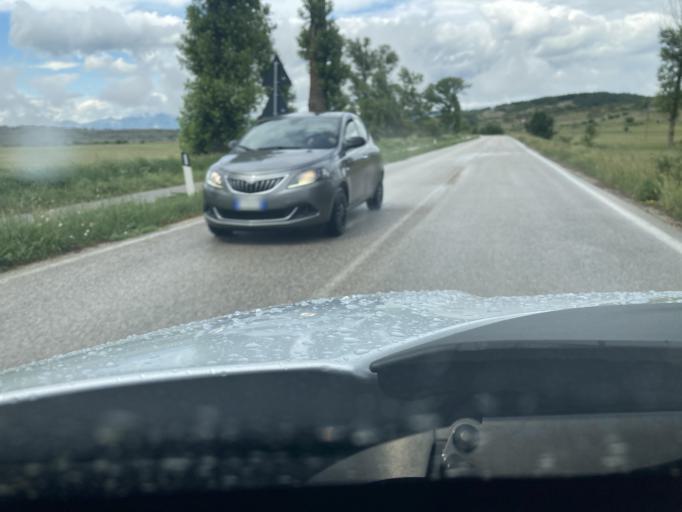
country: IT
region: Abruzzo
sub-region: Provincia dell' Aquila
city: Rocca di Mezzo
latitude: 42.2158
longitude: 13.5297
